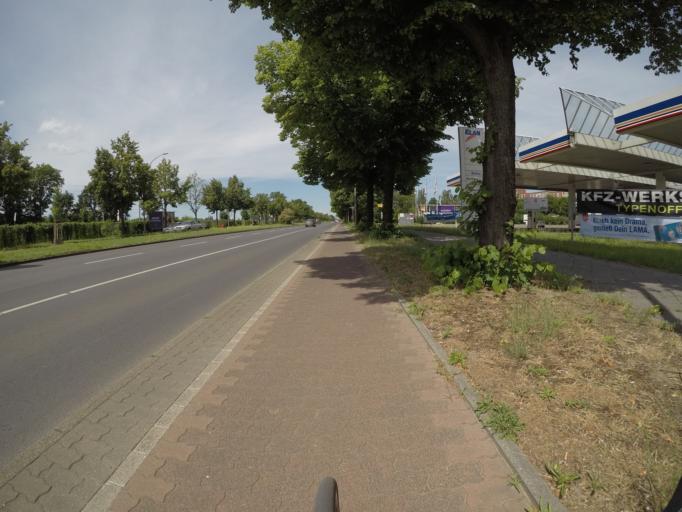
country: DE
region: Berlin
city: Adlershof
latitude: 52.4412
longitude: 13.5331
